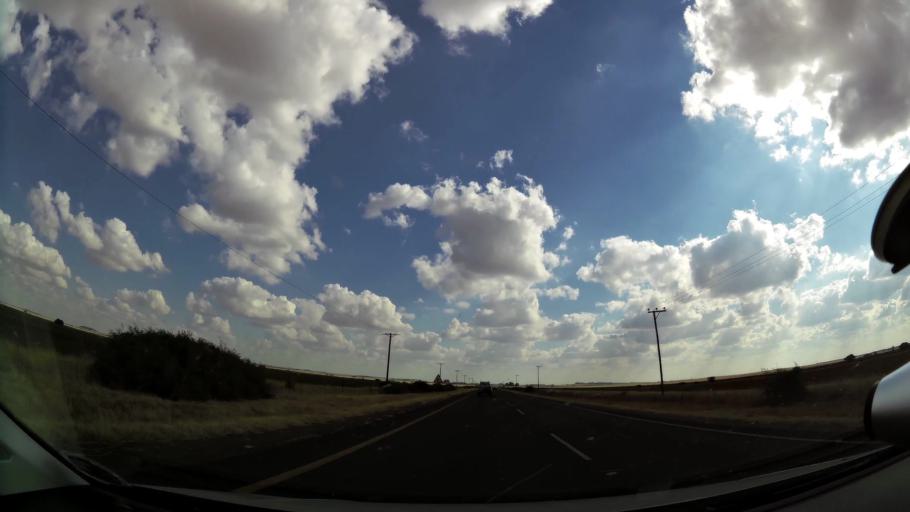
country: ZA
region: Orange Free State
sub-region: Xhariep District Municipality
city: Koffiefontein
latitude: -29.1307
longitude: 25.5211
